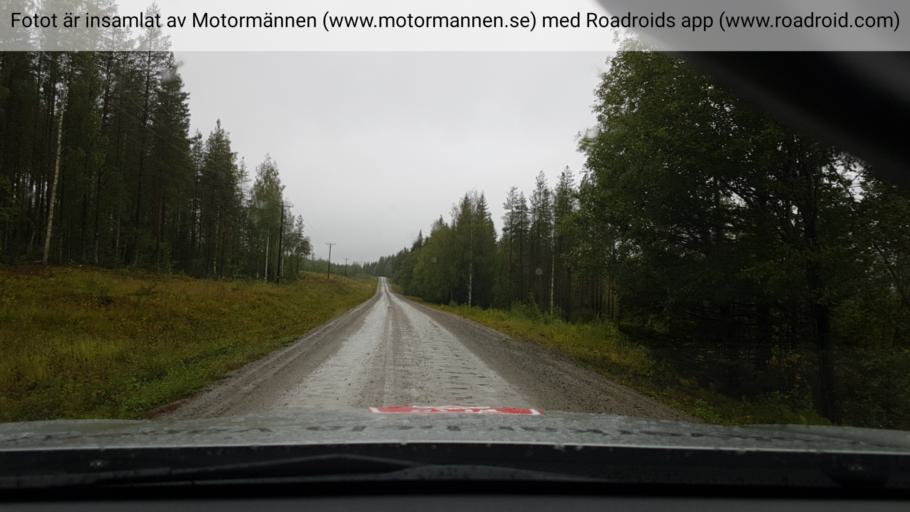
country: SE
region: Vaesterbotten
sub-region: Asele Kommun
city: Insjon
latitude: 64.0884
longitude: 17.8667
